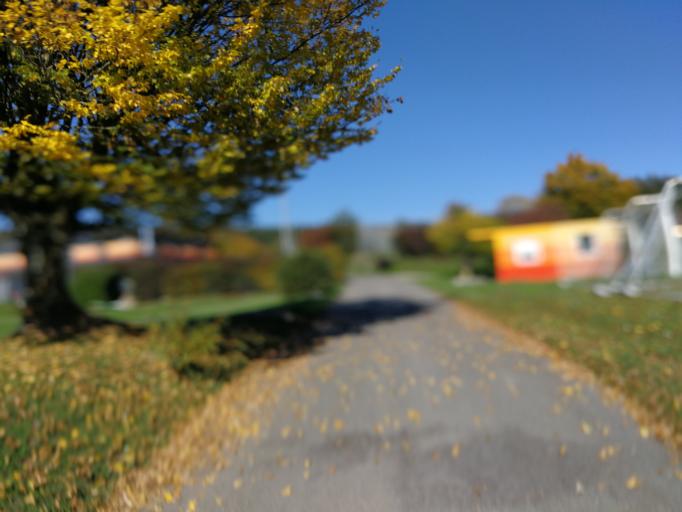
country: CH
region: Zurich
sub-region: Bezirk Meilen
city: Dorf
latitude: 47.2461
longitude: 8.7373
